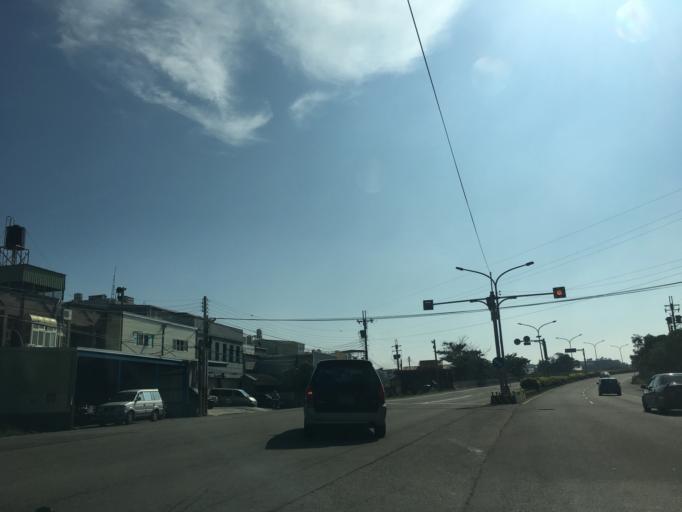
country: TW
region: Taiwan
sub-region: Hsinchu
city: Hsinchu
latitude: 24.8127
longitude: 120.9221
